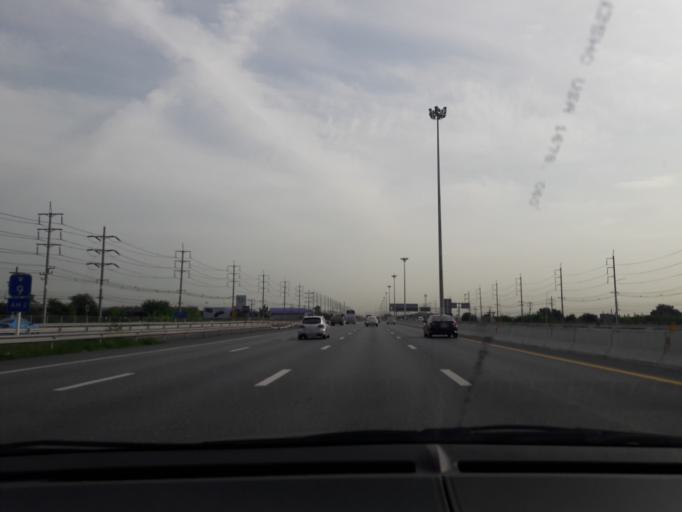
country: TH
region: Pathum Thani
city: Lam Luk Ka
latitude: 13.9398
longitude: 100.7095
